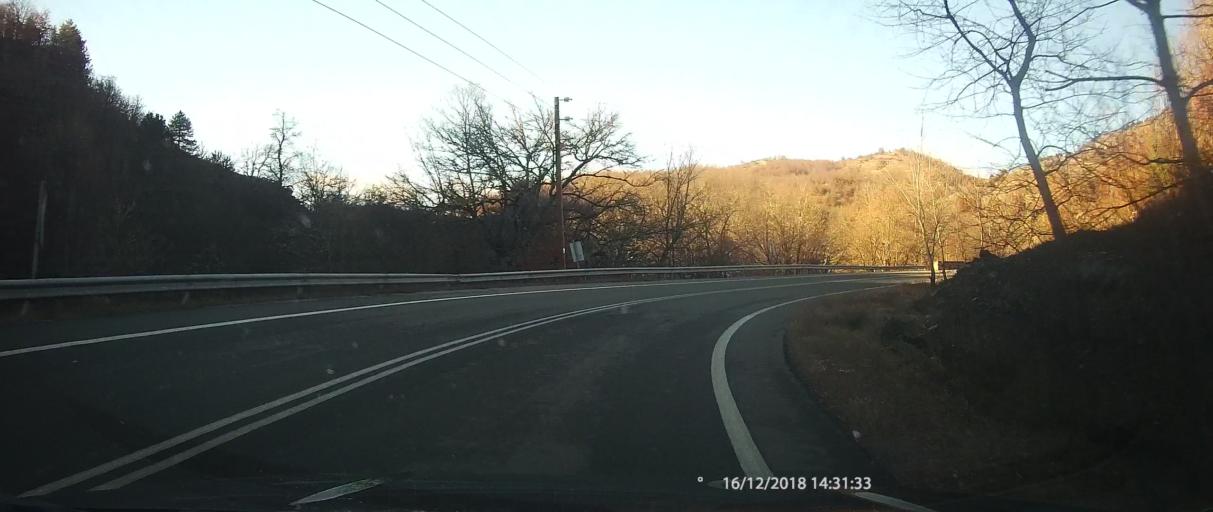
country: GR
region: West Macedonia
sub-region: Nomos Kozanis
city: Tsotili
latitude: 40.1926
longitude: 21.1787
